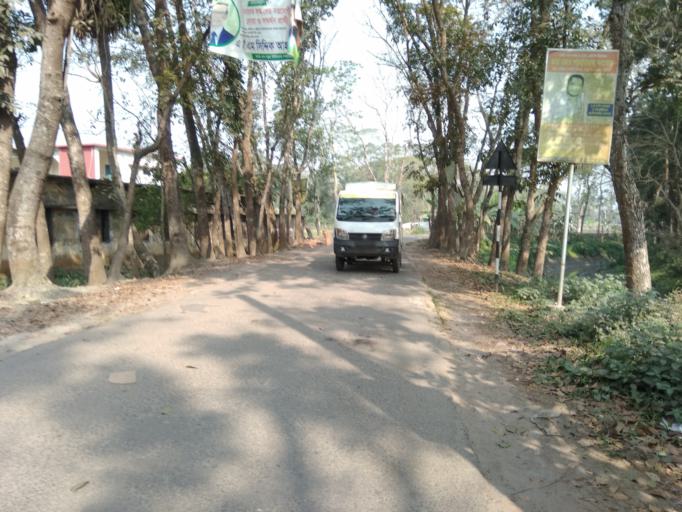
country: BD
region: Barisal
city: Mehendiganj
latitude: 22.9567
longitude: 90.4145
